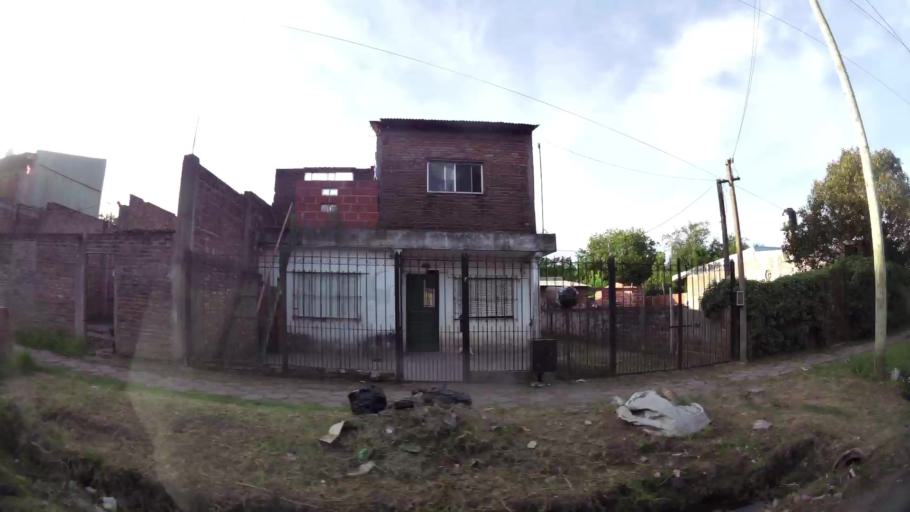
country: AR
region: Buenos Aires
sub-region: Partido de Almirante Brown
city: Adrogue
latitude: -34.7878
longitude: -58.3384
